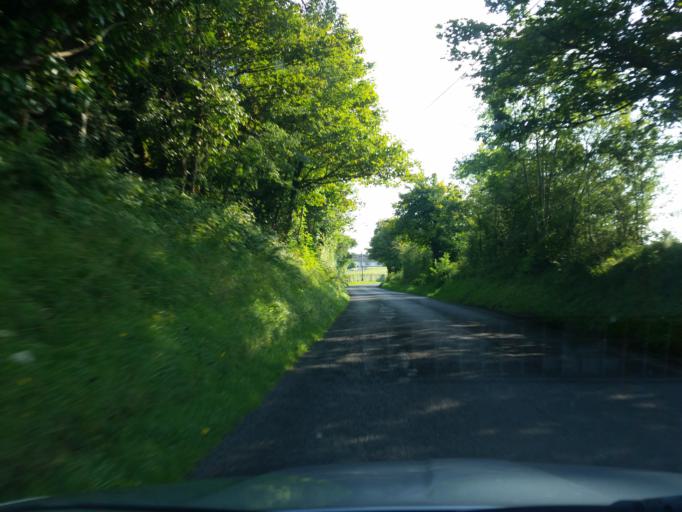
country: GB
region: Northern Ireland
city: Lisnaskea
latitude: 54.2502
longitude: -7.3878
